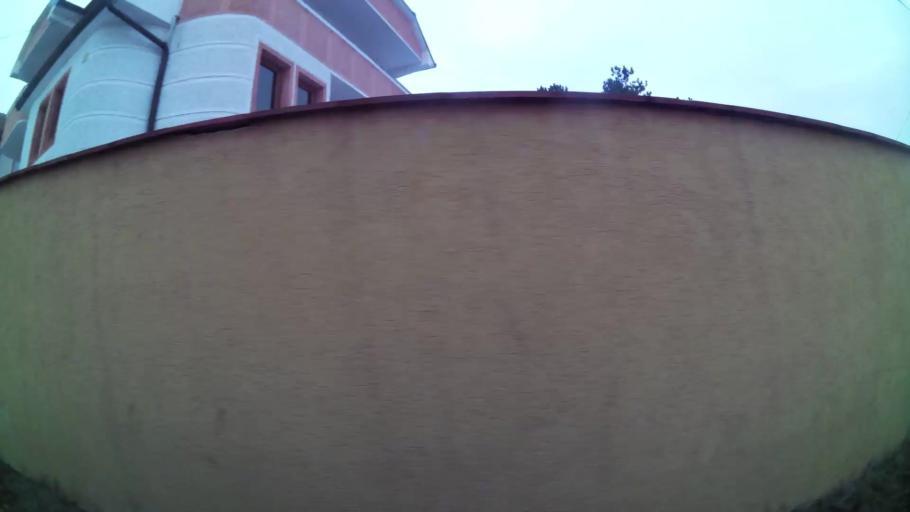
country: MK
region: Suto Orizari
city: Suto Orizare
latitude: 42.0413
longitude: 21.4286
